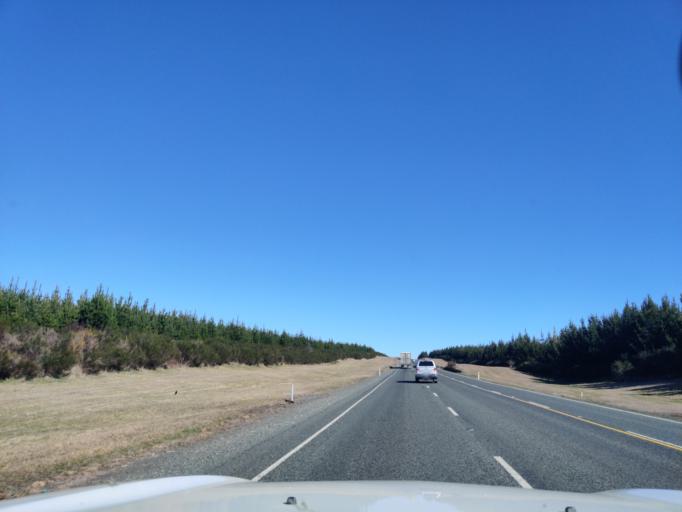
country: NZ
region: Waikato
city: Turangi
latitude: -39.1285
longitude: 175.7912
